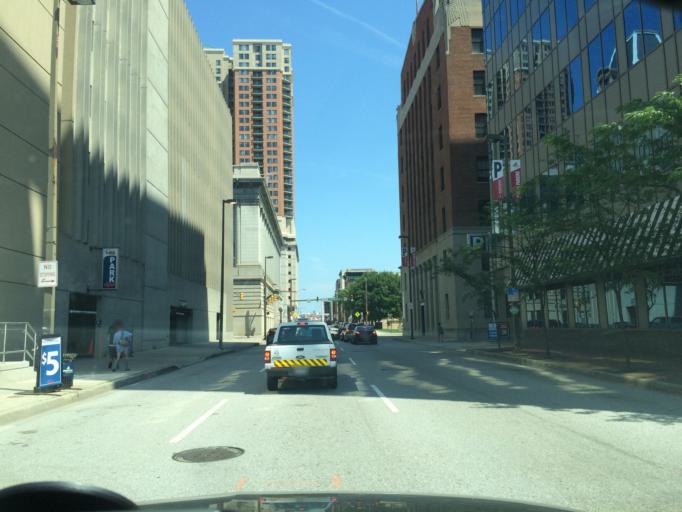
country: US
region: Maryland
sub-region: City of Baltimore
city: Baltimore
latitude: 39.2869
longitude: -76.6087
